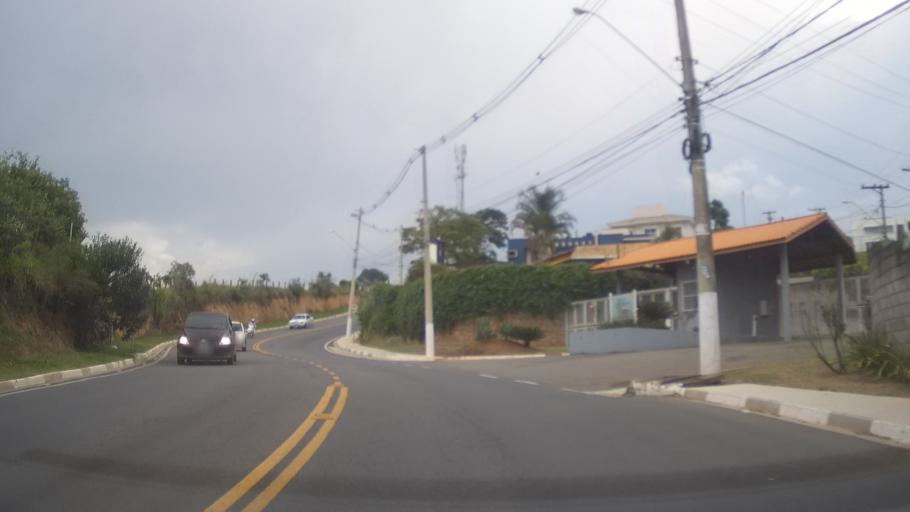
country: BR
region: Sao Paulo
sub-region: Itupeva
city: Itupeva
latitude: -23.1636
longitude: -47.0731
